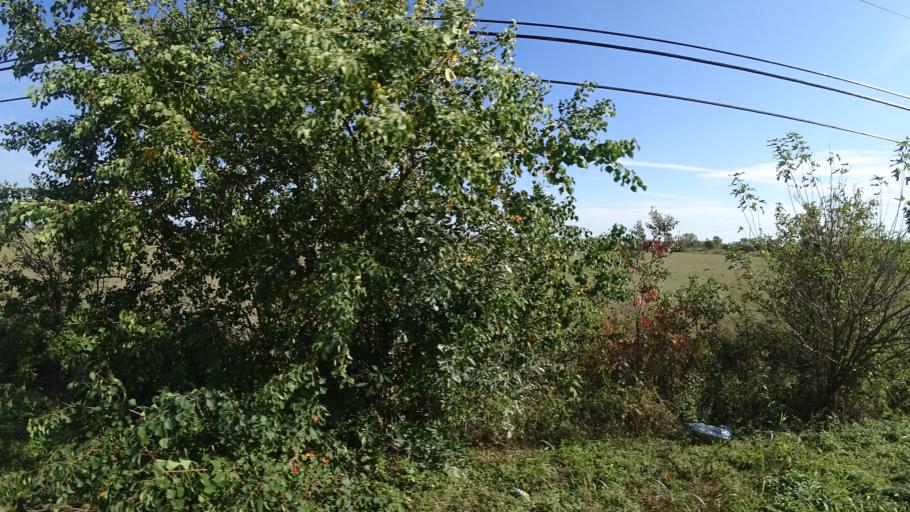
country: US
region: Texas
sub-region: Travis County
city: Pflugerville
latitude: 30.4066
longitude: -97.6277
